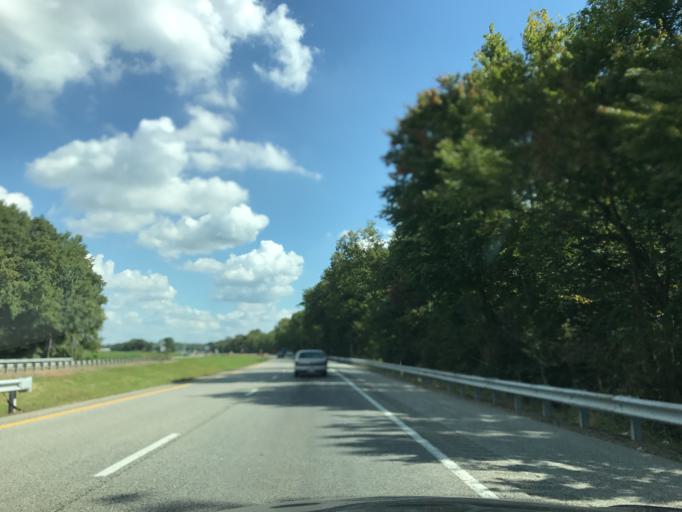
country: US
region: Maryland
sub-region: Queen Anne's County
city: Centreville
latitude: 39.0199
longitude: -76.0397
